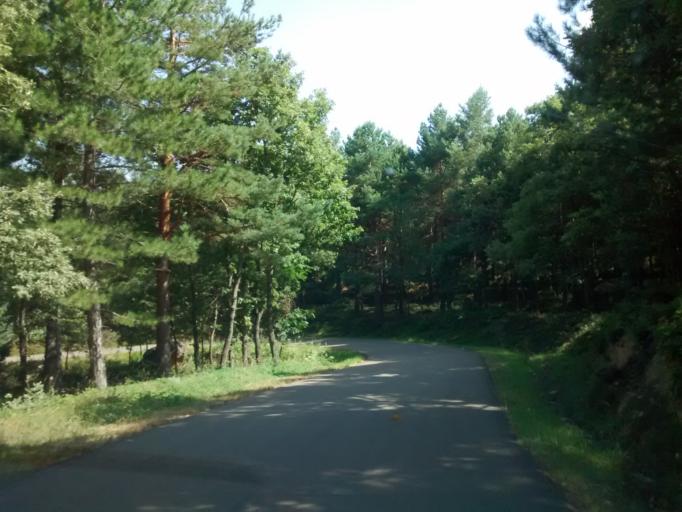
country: ES
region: Aragon
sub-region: Provincia de Zaragoza
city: Lituenigo
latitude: 41.8096
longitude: -1.8002
